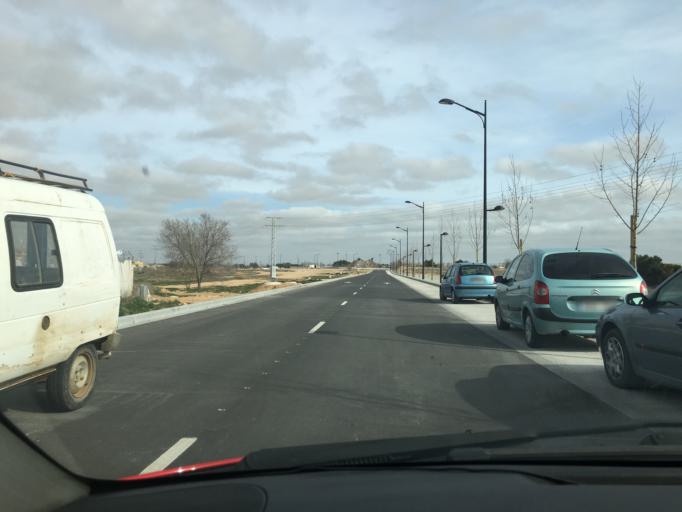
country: ES
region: Castille-La Mancha
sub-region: Provincia de Albacete
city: Albacete
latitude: 38.9853
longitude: -1.8418
